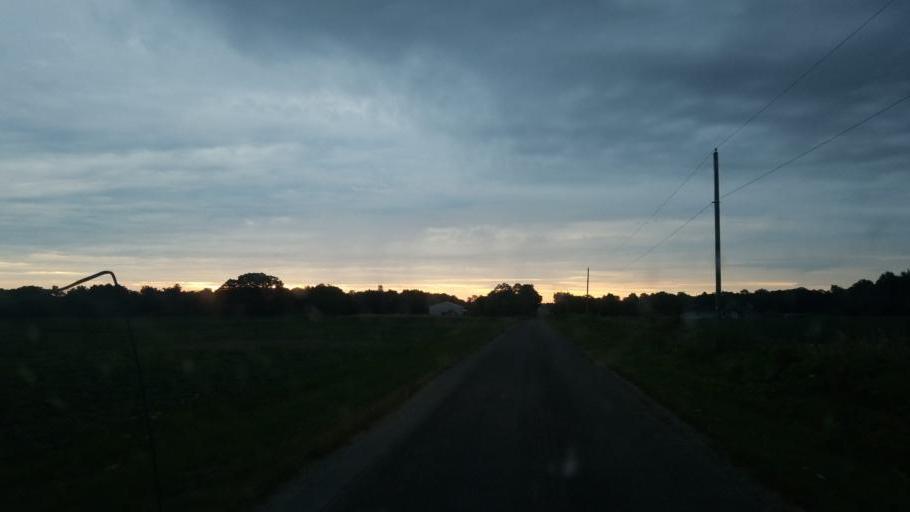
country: US
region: Ohio
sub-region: Defiance County
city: Hicksville
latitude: 41.3681
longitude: -84.8022
